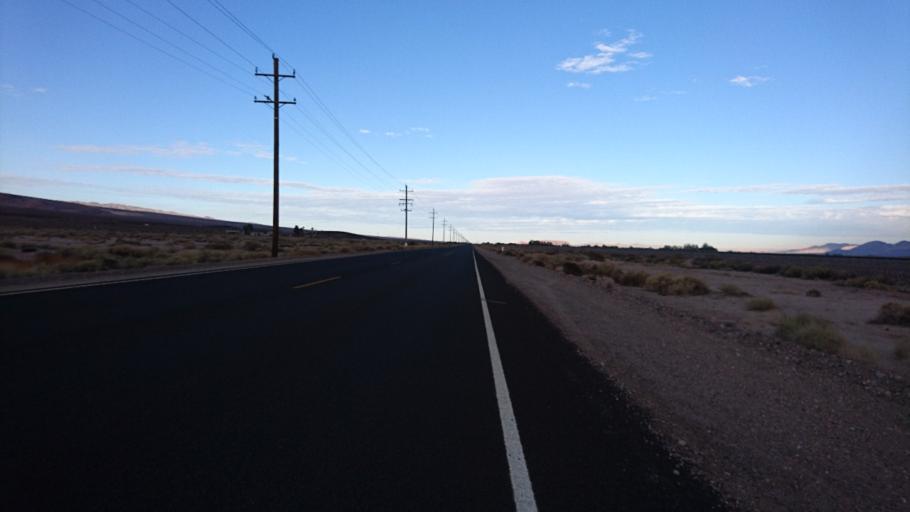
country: US
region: California
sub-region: San Bernardino County
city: Barstow
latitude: 34.8365
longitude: -116.7159
